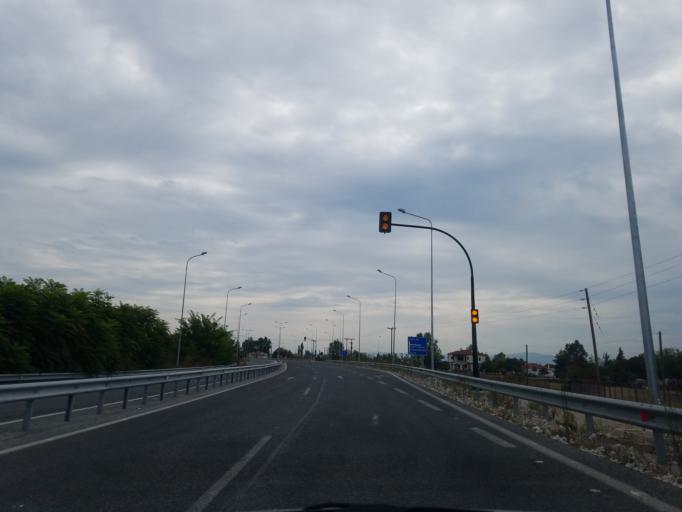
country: GR
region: Thessaly
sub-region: Nomos Kardhitsas
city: Sofades
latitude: 39.3034
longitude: 22.1272
